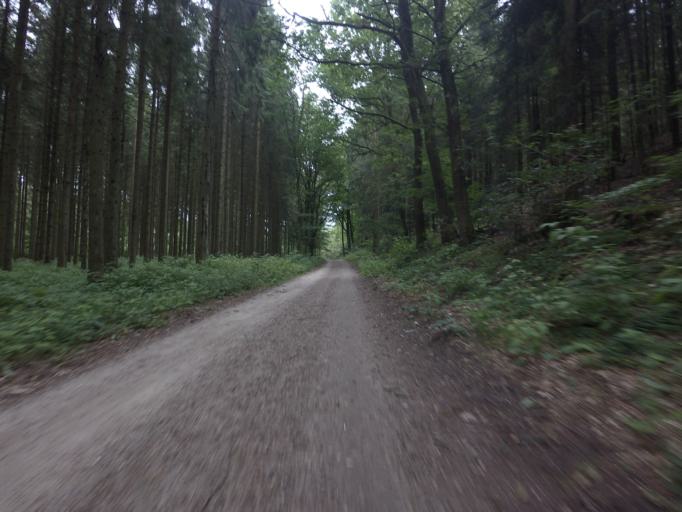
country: DK
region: Central Jutland
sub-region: Horsens Kommune
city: Braedstrup
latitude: 56.0219
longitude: 9.5016
